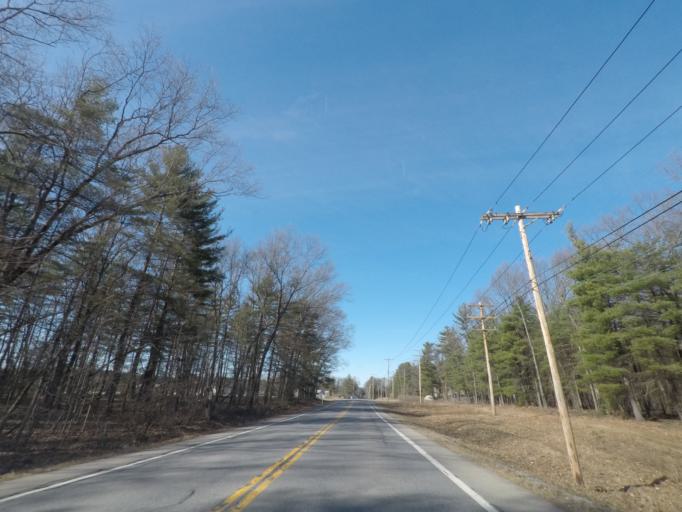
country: US
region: New York
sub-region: Saratoga County
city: Milton
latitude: 43.0567
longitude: -73.8505
